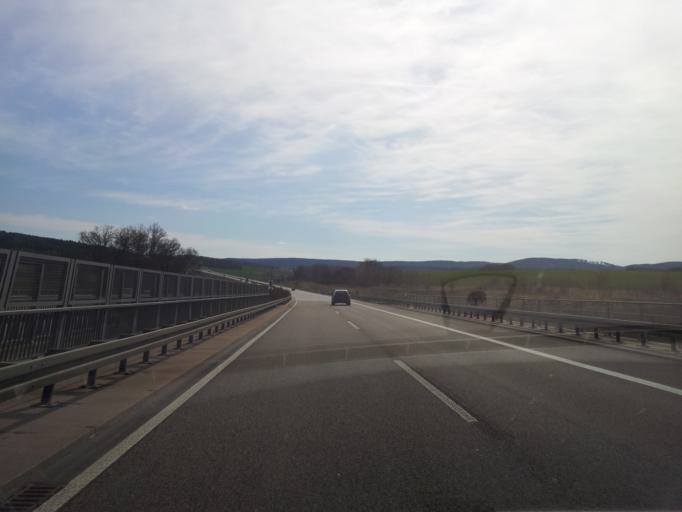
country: DE
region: Thuringia
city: Ritschenhausen
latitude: 50.5050
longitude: 10.4443
